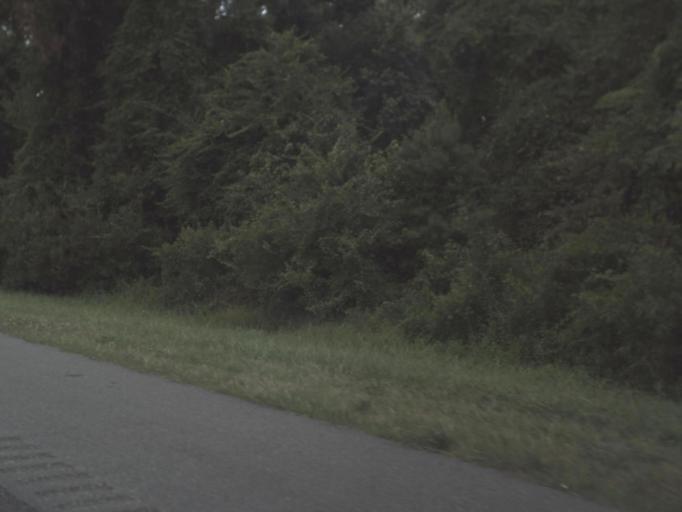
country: US
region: Florida
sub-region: Alachua County
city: High Springs
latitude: 29.9491
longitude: -82.5680
